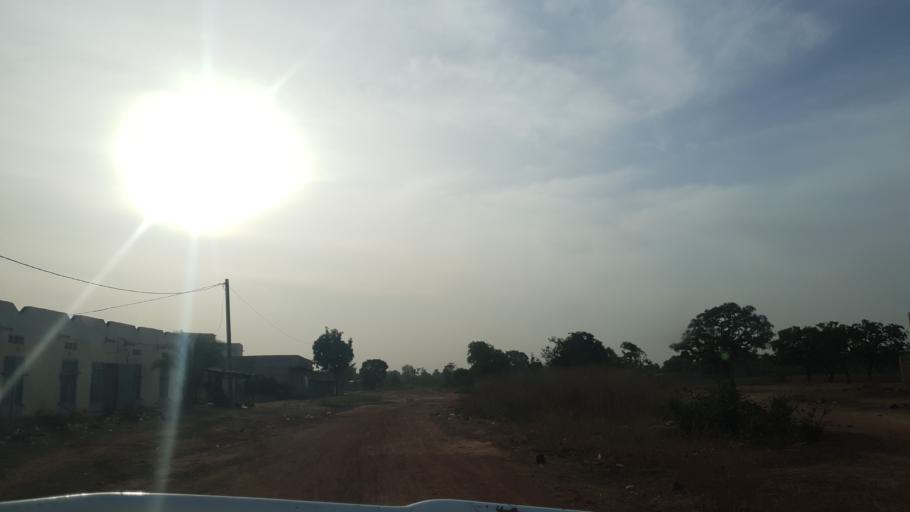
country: ML
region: Segou
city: Baroueli
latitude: 12.7735
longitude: -6.9366
